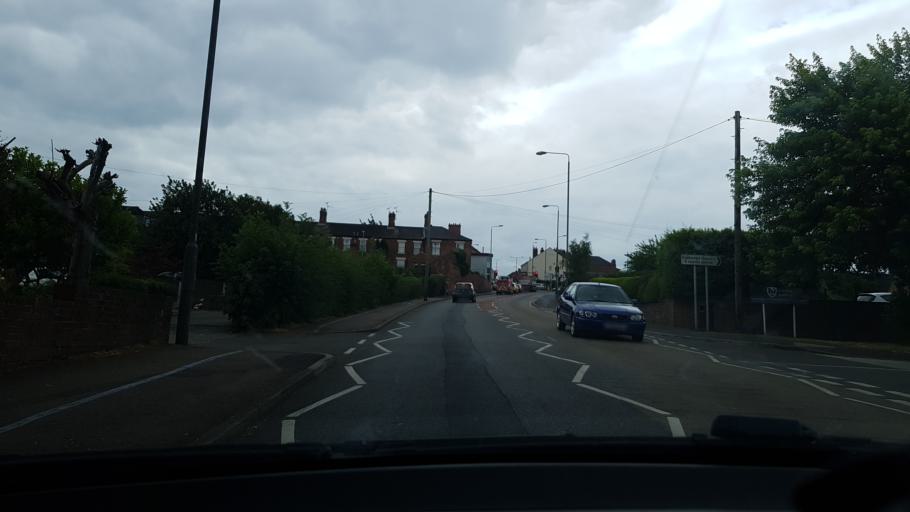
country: GB
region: England
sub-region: Nottinghamshire
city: Eastwood
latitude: 53.0204
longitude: -1.3079
